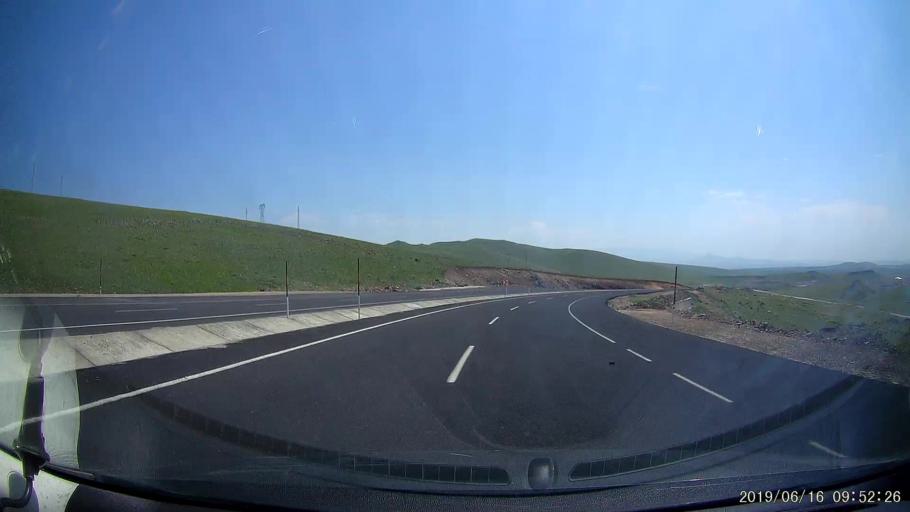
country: TR
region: Kars
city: Digor
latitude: 40.3940
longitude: 43.3866
